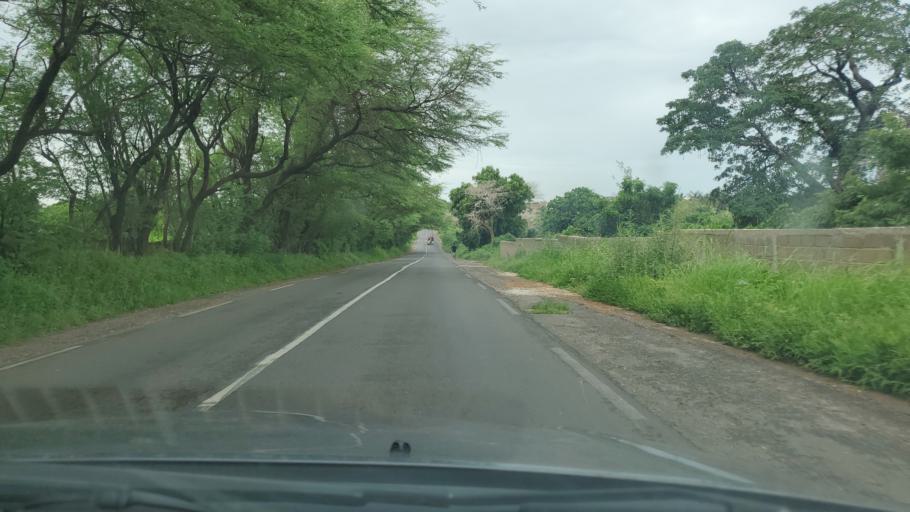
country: SN
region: Thies
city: Mekhe
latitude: 15.1261
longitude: -16.8645
